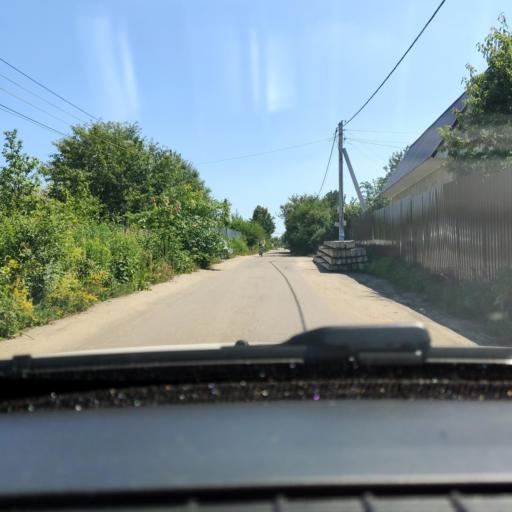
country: RU
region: Voronezj
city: Shilovo
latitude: 51.5910
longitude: 39.1490
